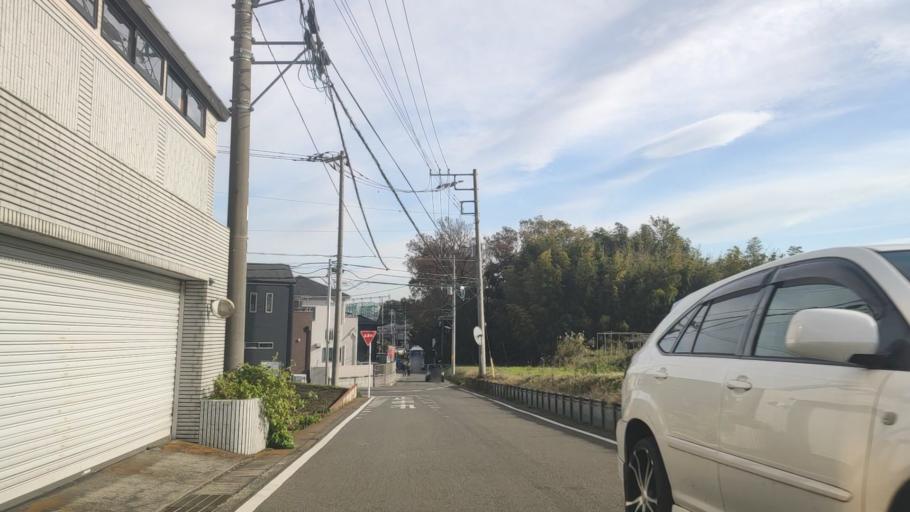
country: JP
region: Kanagawa
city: Atsugi
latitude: 35.4311
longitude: 139.3945
